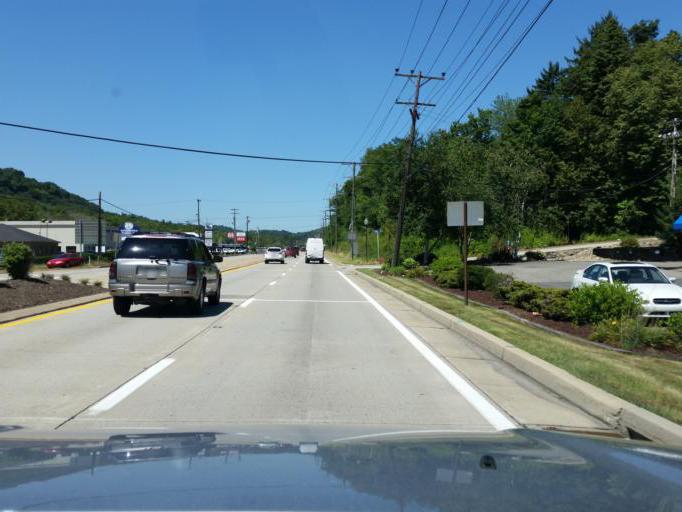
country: US
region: Pennsylvania
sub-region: Westmoreland County
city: Murrysville
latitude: 40.4259
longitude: -79.6741
